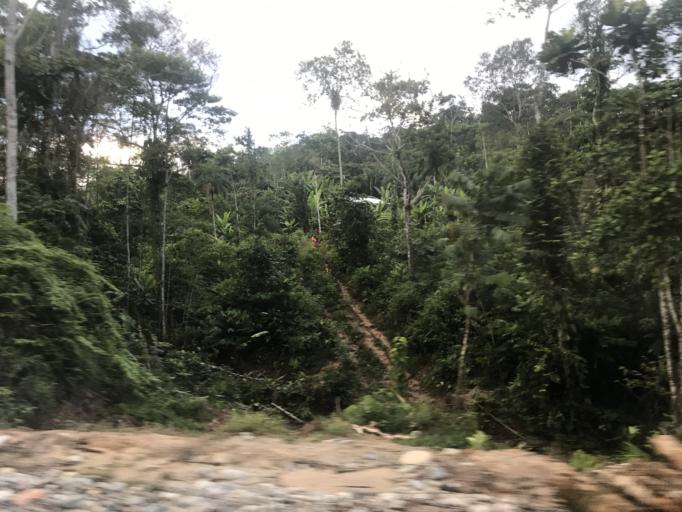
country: EC
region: Napo
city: Tena
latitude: -1.0612
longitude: -77.7012
